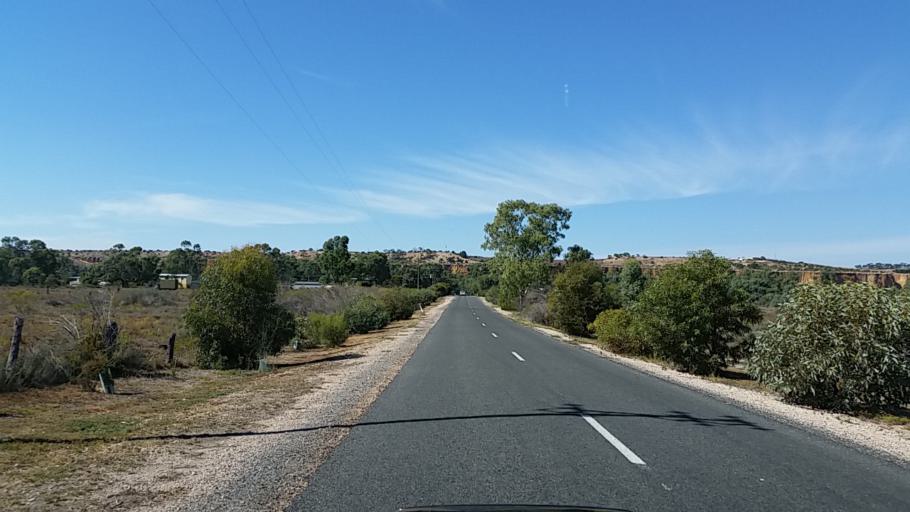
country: AU
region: South Australia
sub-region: Mid Murray
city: Mannum
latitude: -34.7061
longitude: 139.5695
